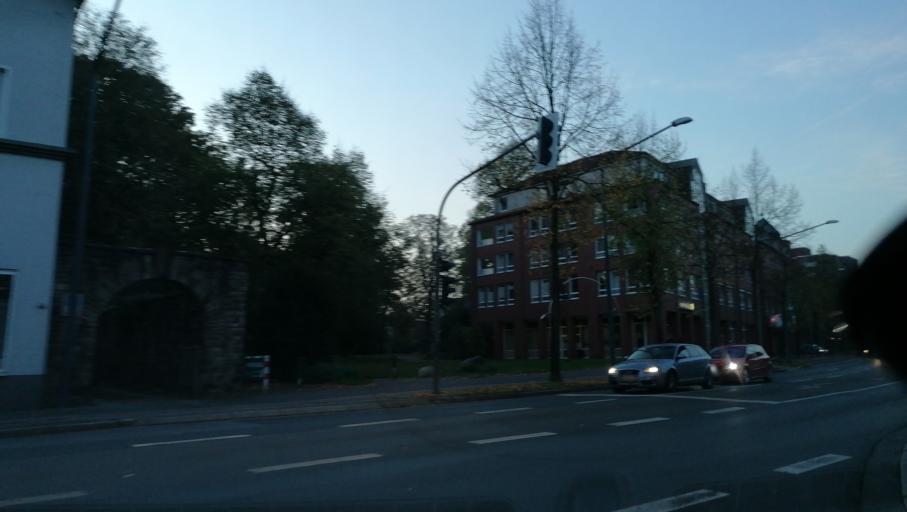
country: DE
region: North Rhine-Westphalia
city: Herten
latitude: 51.5903
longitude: 7.1422
